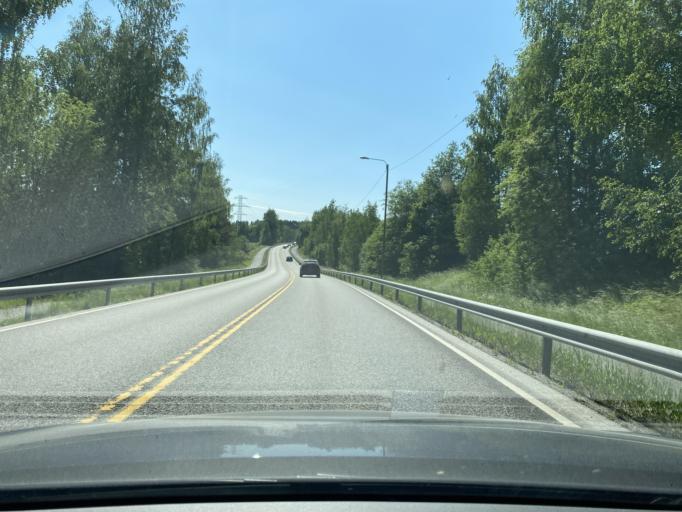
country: FI
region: Pirkanmaa
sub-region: Tampere
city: Nokia
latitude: 61.4736
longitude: 23.5315
